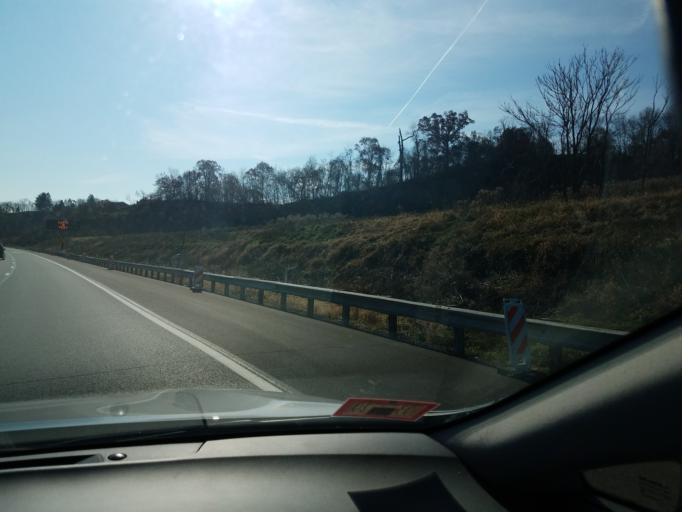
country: US
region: Pennsylvania
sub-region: Allegheny County
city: West View
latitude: 40.5139
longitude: -80.0519
